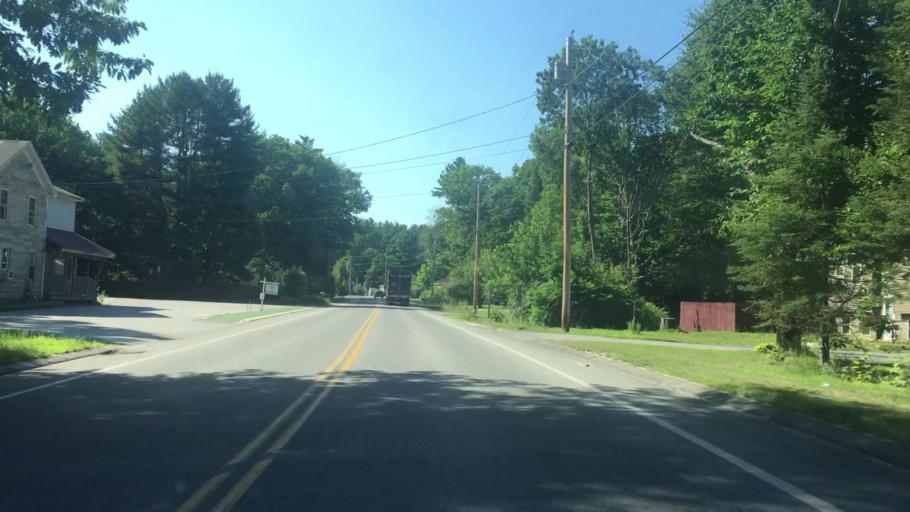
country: US
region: Maine
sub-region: York County
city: Buxton
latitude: 43.5875
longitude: -70.5195
